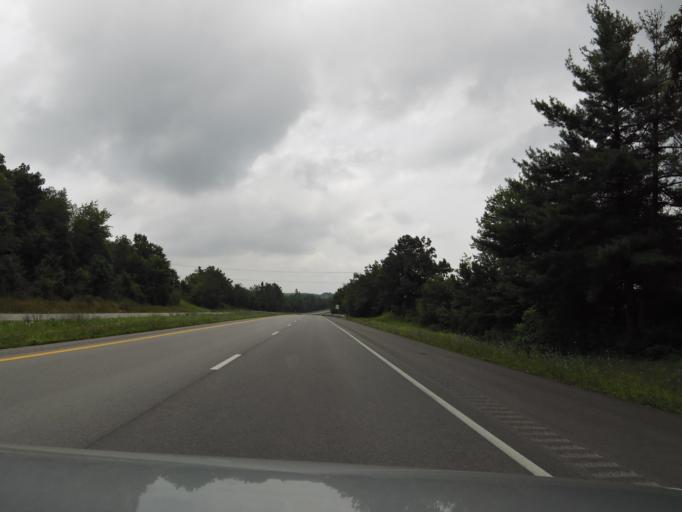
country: US
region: Kentucky
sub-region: Grayson County
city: Leitchfield
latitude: 37.4474
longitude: -86.3436
